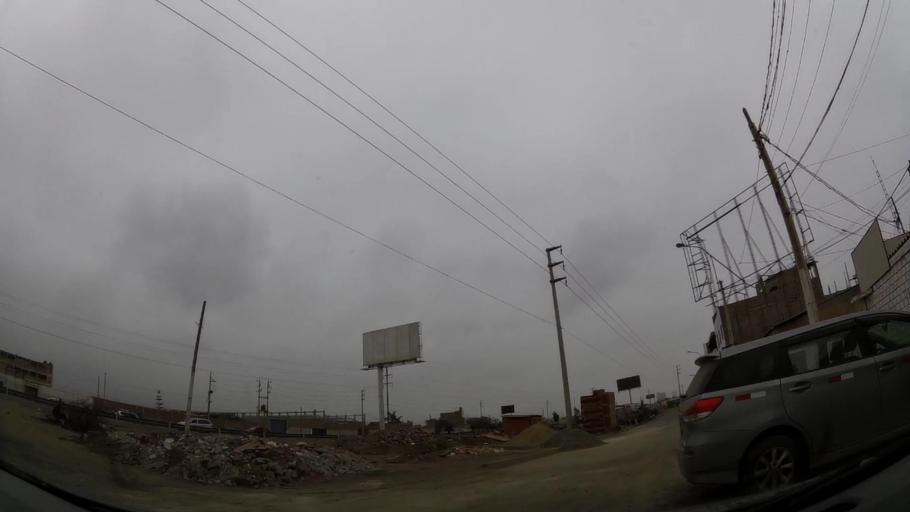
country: PE
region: Lima
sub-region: Lima
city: Punta Hermosa
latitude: -12.3064
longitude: -76.8387
